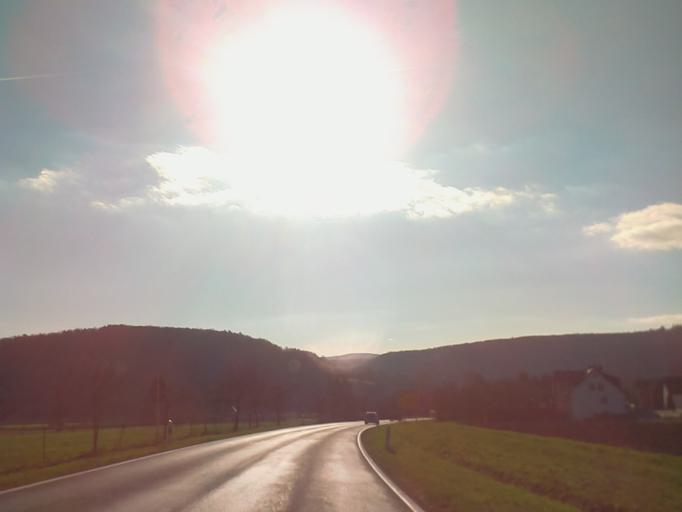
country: DE
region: Bavaria
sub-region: Regierungsbezirk Unterfranken
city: Bad Bocklet
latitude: 50.2613
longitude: 10.0687
